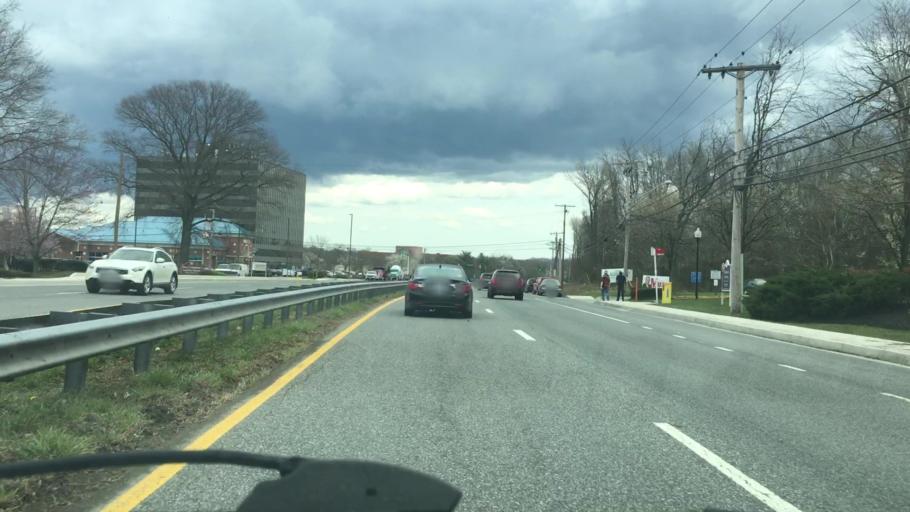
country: US
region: Maryland
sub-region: Prince George's County
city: Glenn Dale
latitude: 38.9910
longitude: -76.8315
